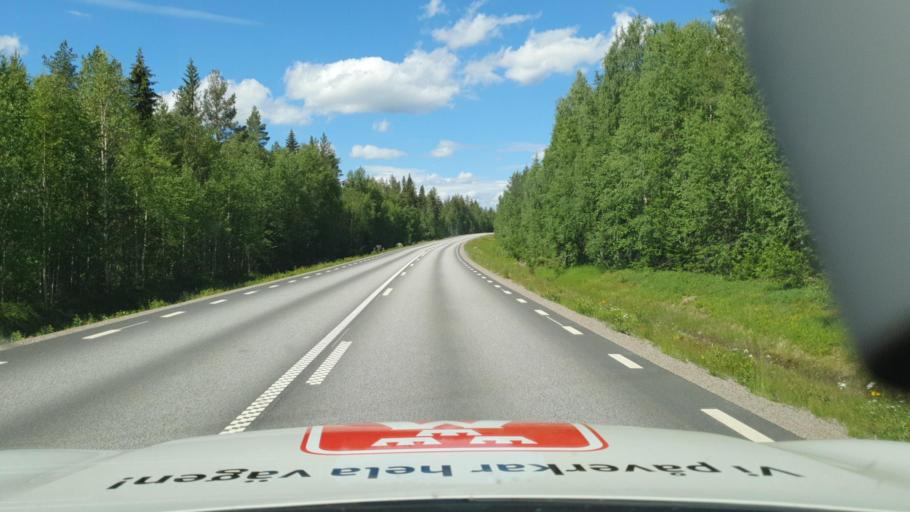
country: SE
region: Vaesterbotten
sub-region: Skelleftea Kommun
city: Boliden
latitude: 64.9065
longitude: 20.3491
